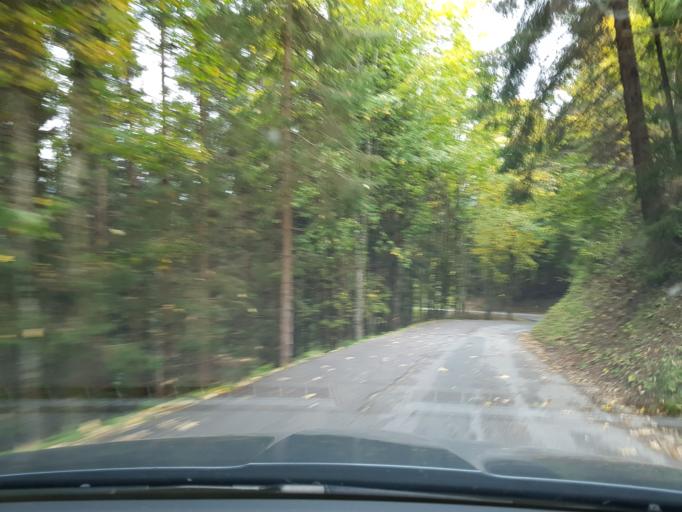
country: AT
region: Salzburg
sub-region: Politischer Bezirk Sankt Johann im Pongau
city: Radstadt
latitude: 47.3896
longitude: 13.4778
